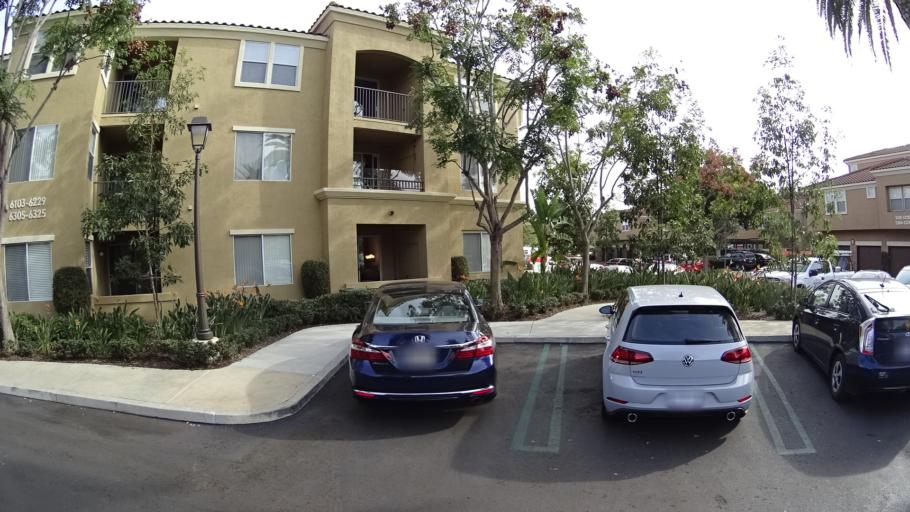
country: US
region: California
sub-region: Orange County
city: Laguna Woods
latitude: 33.5951
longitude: -117.7338
